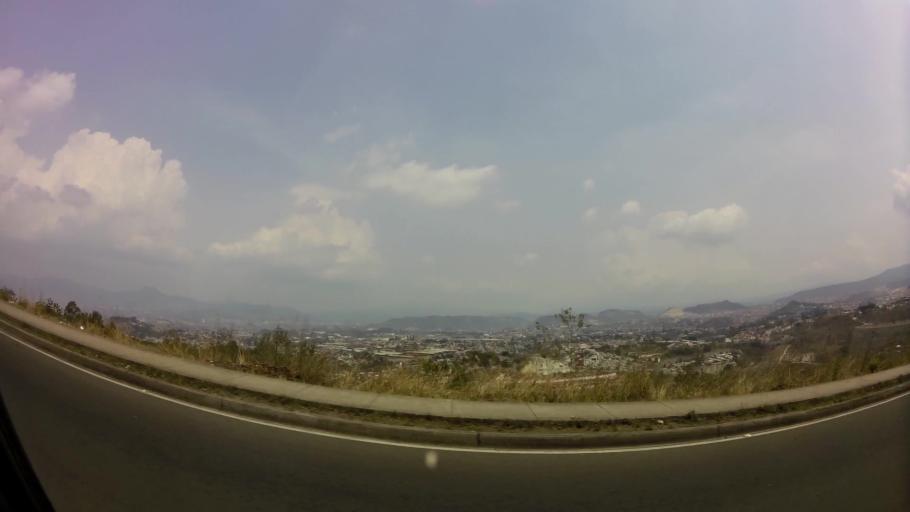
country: HN
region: Francisco Morazan
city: Tegucigalpa
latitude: 14.0743
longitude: -87.2375
